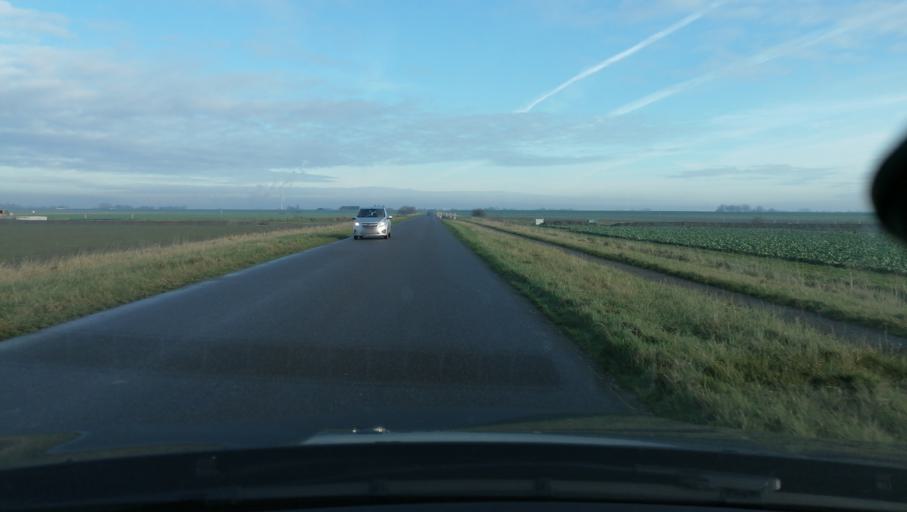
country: DE
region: Schleswig-Holstein
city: Friedrichsgabekoog
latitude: 54.1189
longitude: 8.9737
